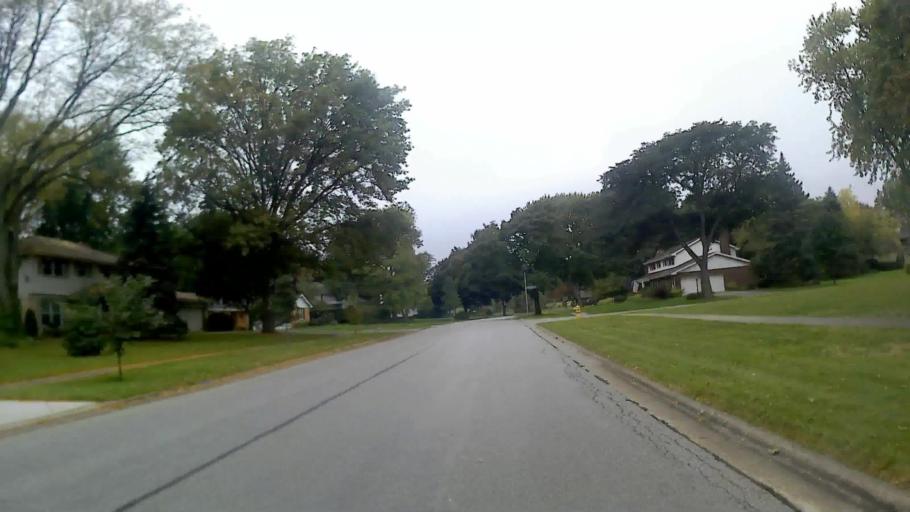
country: US
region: Illinois
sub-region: DuPage County
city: Wheaton
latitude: 41.8447
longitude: -88.1033
